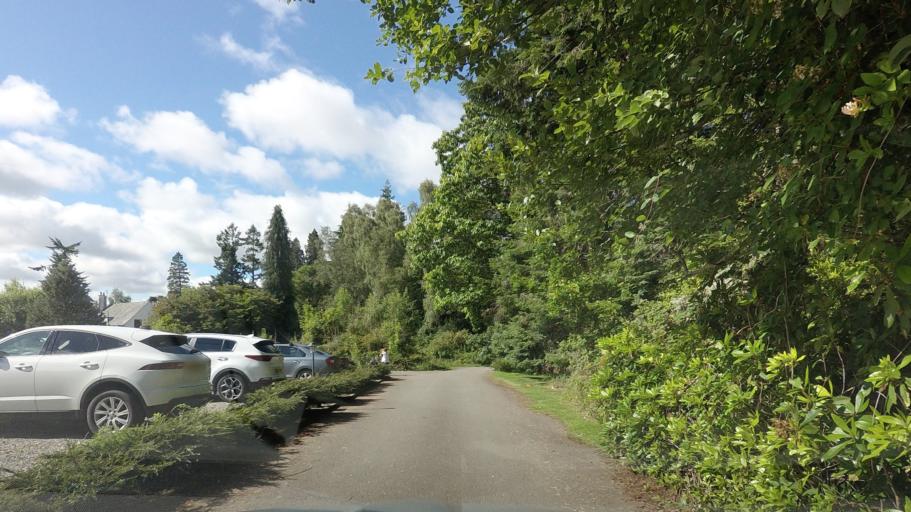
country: GB
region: Scotland
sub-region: Stirling
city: Killearn
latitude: 56.0682
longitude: -4.4801
